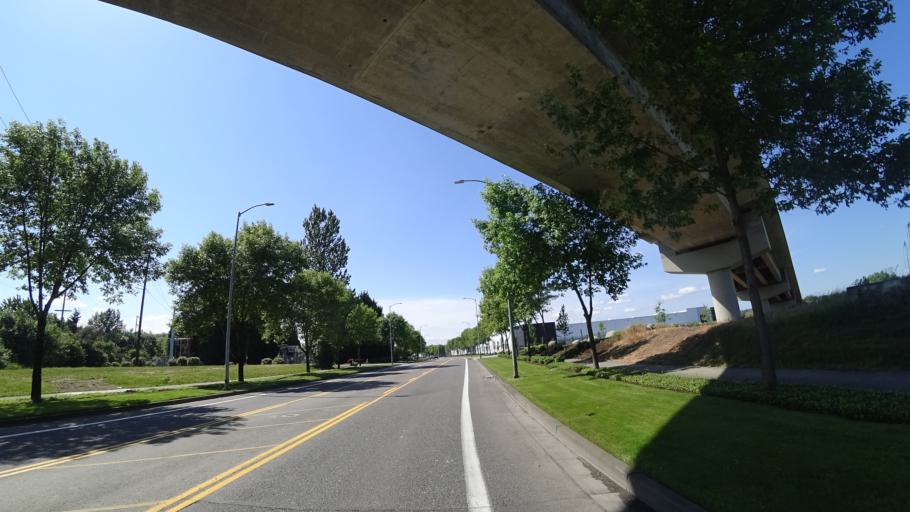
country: US
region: Oregon
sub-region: Multnomah County
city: Lents
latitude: 45.5673
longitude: -122.5565
